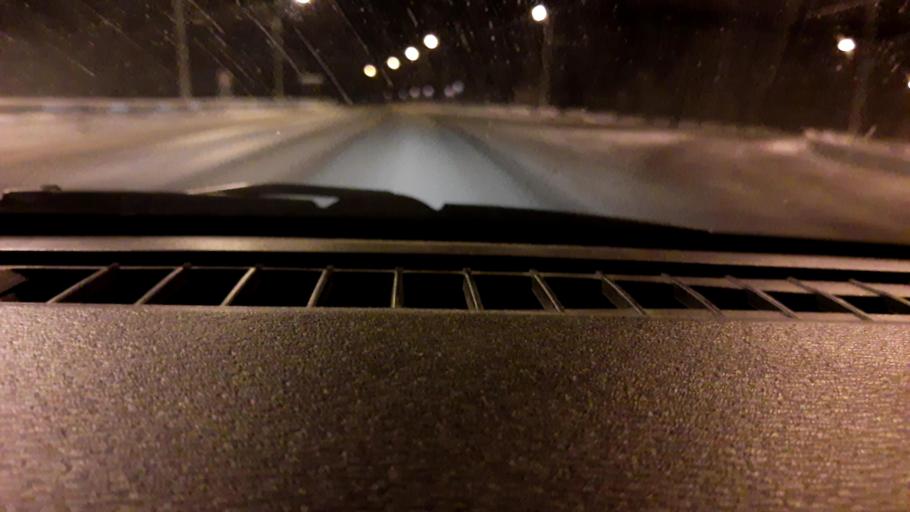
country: RU
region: Nizjnij Novgorod
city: Sitniki
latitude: 56.4693
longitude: 44.0365
